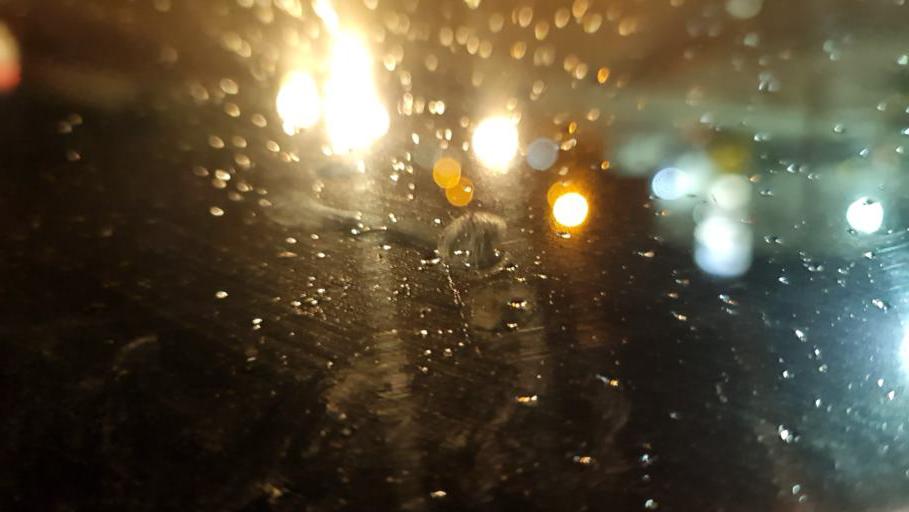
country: MZ
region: Nampula
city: Nampula
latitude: -15.1125
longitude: 39.2854
